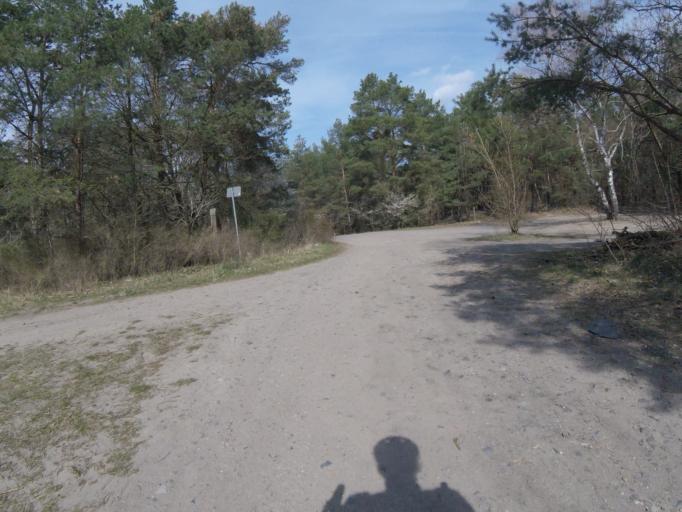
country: DE
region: Brandenburg
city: Bestensee
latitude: 52.2216
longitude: 13.6615
